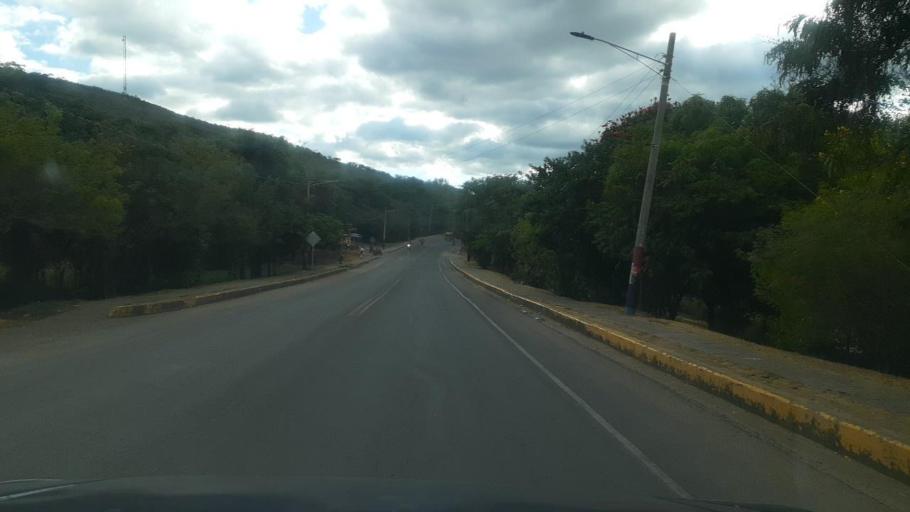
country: NI
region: Madriz
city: Somoto
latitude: 13.4804
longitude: -86.5870
